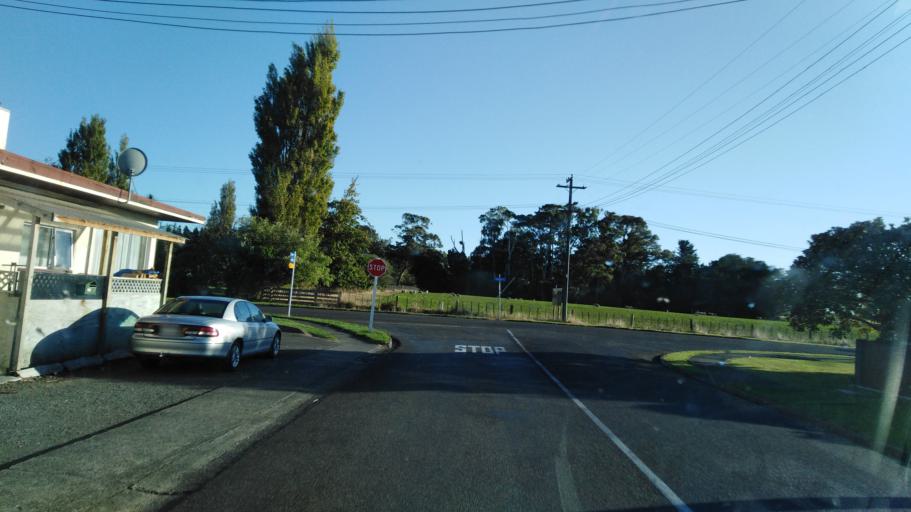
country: NZ
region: Manawatu-Wanganui
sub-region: Rangitikei District
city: Bulls
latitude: -40.0643
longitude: 175.3845
